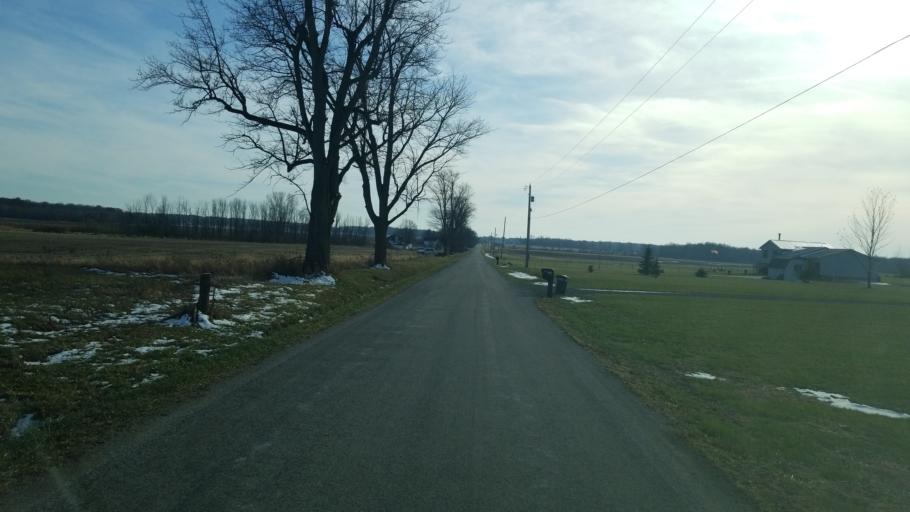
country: US
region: Ohio
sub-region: Huron County
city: New London
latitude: 41.0485
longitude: -82.2800
